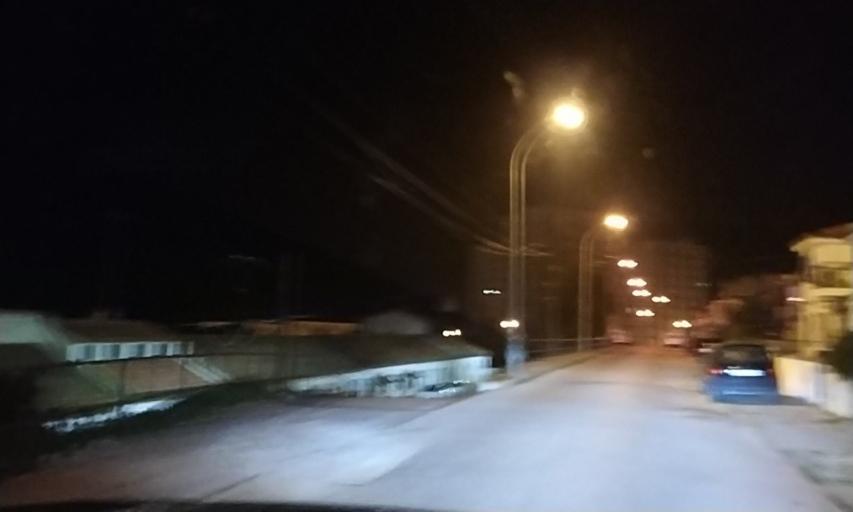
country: PT
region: Setubal
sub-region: Setubal
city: Setubal
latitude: 38.5283
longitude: -8.9050
